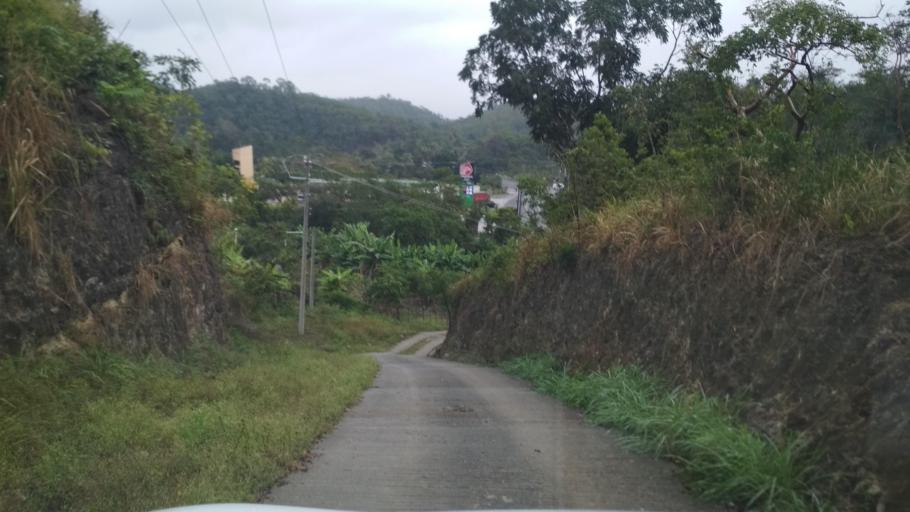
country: MX
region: Veracruz
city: Papantla de Olarte
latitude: 20.4646
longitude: -97.3085
